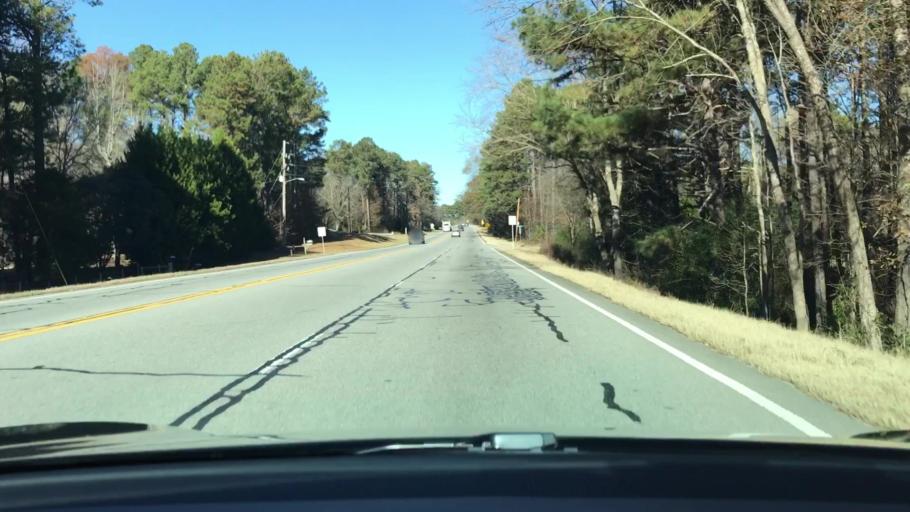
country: US
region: Georgia
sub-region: Barrow County
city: Russell
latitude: 33.9140
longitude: -83.7182
